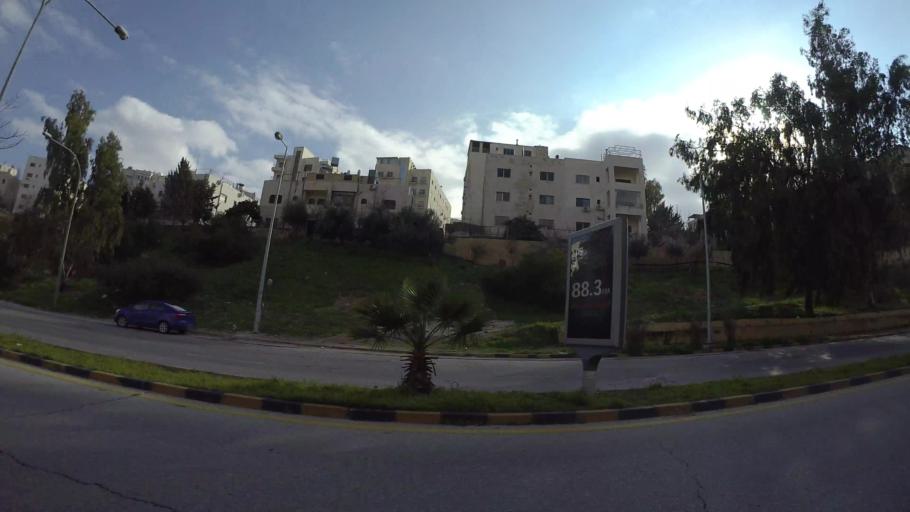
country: JO
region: Amman
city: Amman
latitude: 31.9595
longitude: 35.8996
